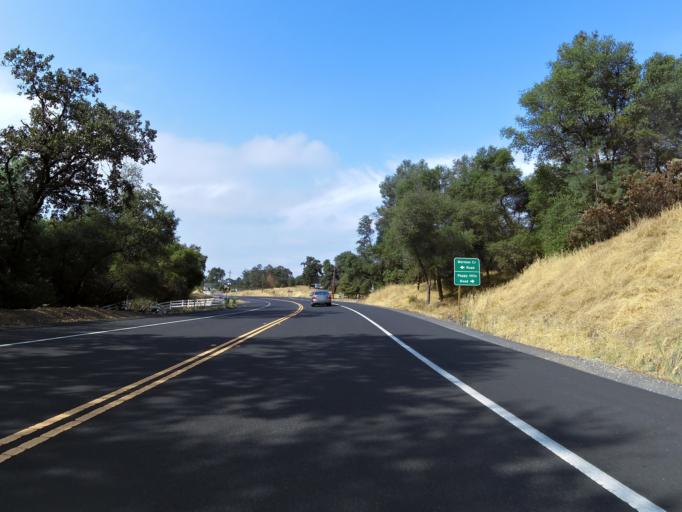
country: US
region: California
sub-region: Tuolumne County
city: Jamestown
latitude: 37.9931
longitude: -120.4368
